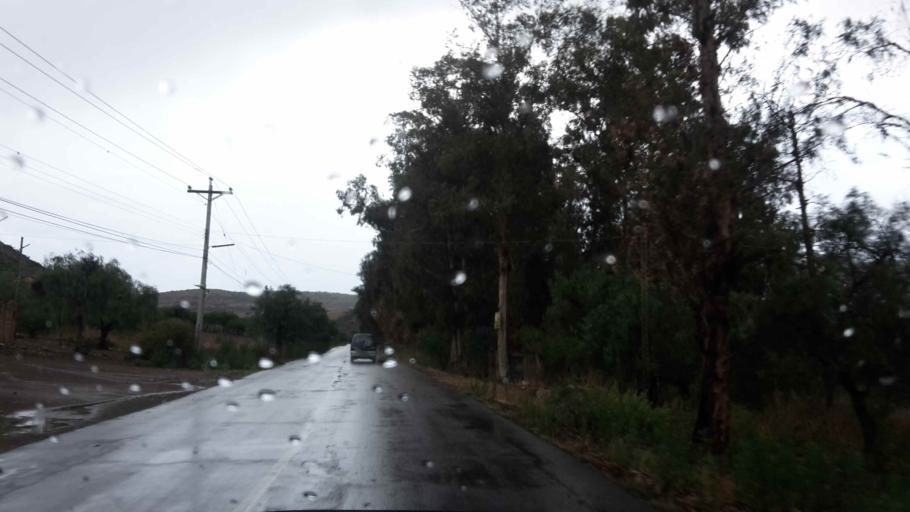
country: BO
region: Cochabamba
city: Tarata
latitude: -17.5403
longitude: -66.1094
